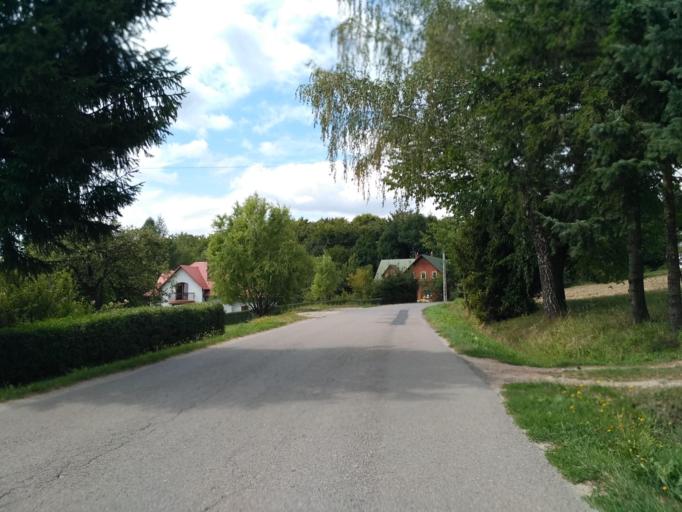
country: PL
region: Subcarpathian Voivodeship
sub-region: Powiat rzeszowski
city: Chmielnik
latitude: 49.9489
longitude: 22.1547
